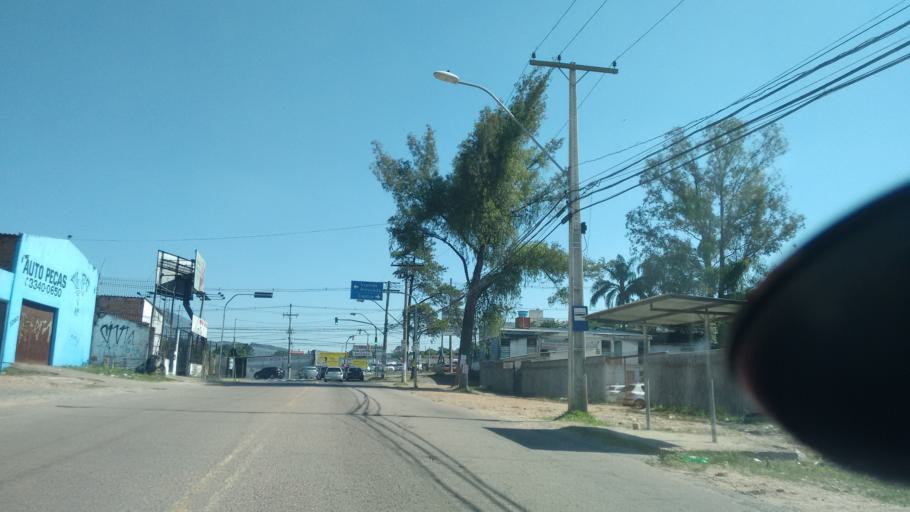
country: BR
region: Rio Grande do Sul
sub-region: Cachoeirinha
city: Cachoeirinha
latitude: -30.0107
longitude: -51.1284
